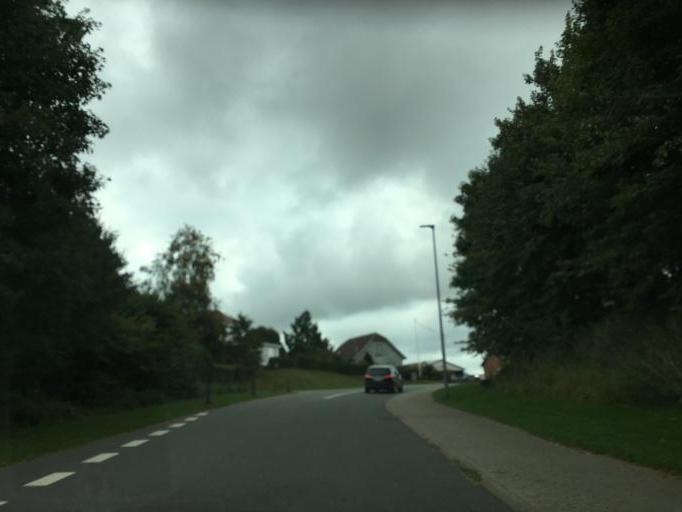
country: DK
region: South Denmark
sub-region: Kolding Kommune
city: Kolding
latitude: 55.5662
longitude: 9.4903
